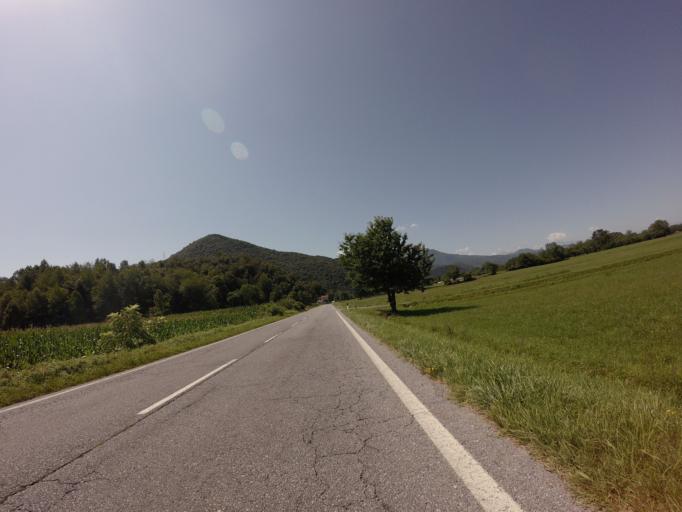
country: IT
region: Piedmont
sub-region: Provincia di Cuneo
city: Chiusa di Pesio
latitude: 44.3346
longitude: 7.6904
